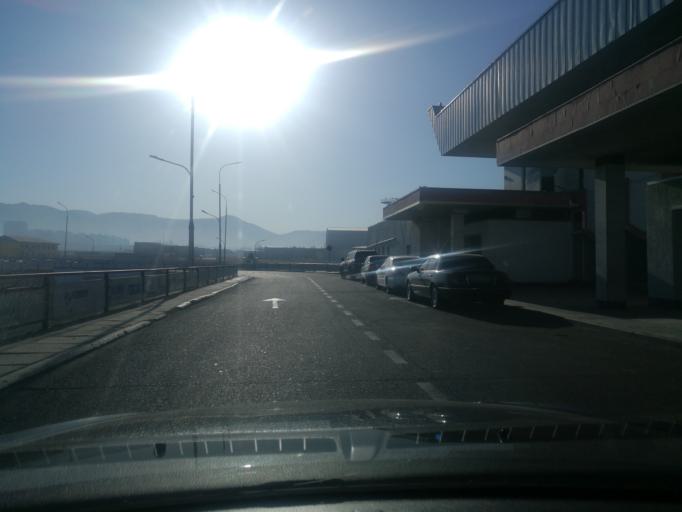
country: MN
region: Ulaanbaatar
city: Ulaanbaatar
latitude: 47.8526
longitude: 106.7634
